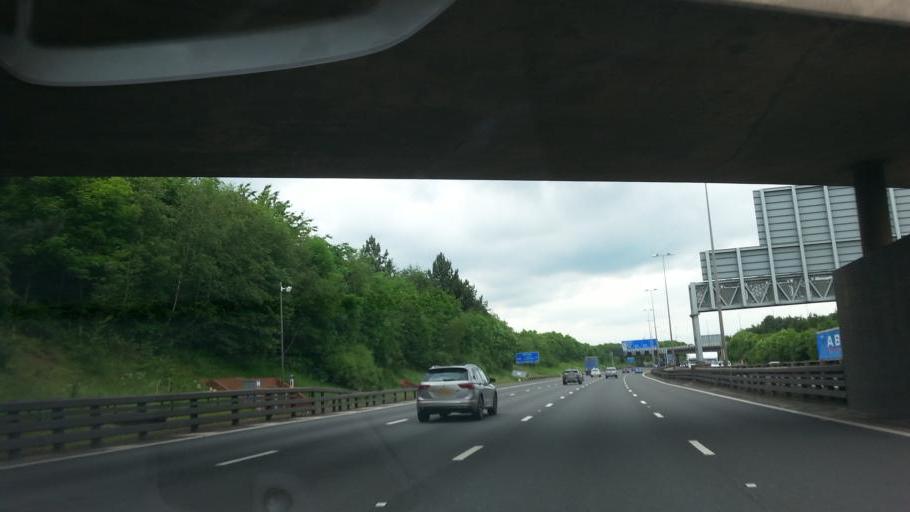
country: GB
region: England
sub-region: Warwickshire
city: Water Orton
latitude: 52.5042
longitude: -1.7228
